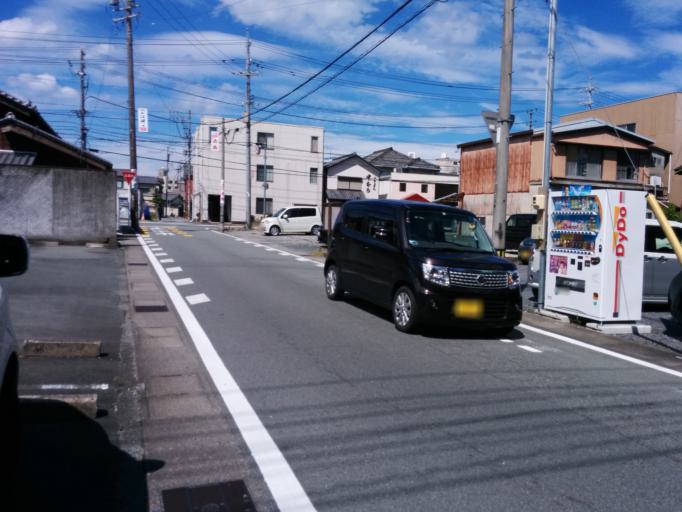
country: JP
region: Mie
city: Ise
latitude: 34.4889
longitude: 136.7049
